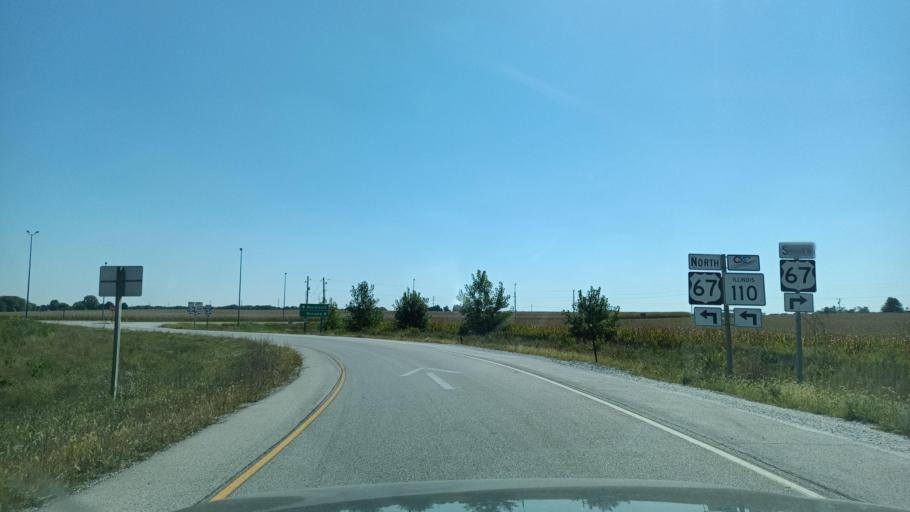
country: US
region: Illinois
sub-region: McDonough County
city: Macomb
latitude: 40.5021
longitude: -90.6762
